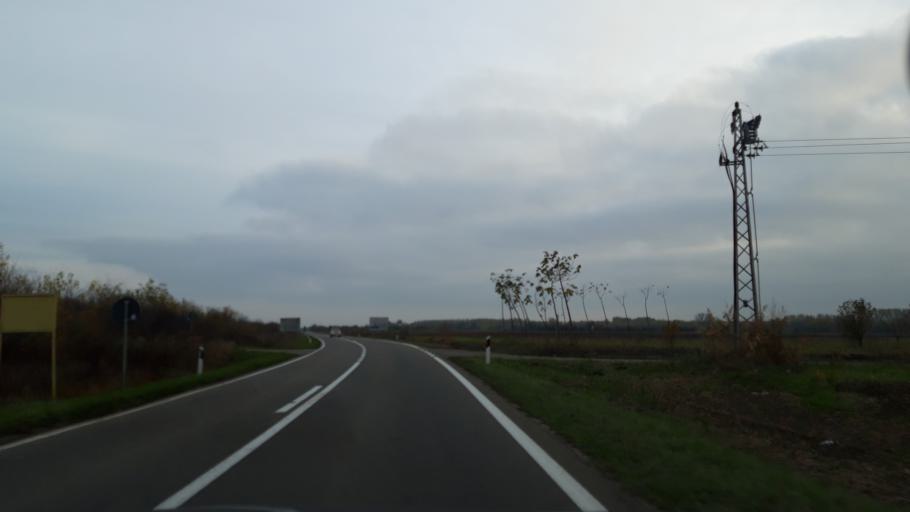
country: RS
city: Sanad
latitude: 45.9998
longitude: 20.1027
